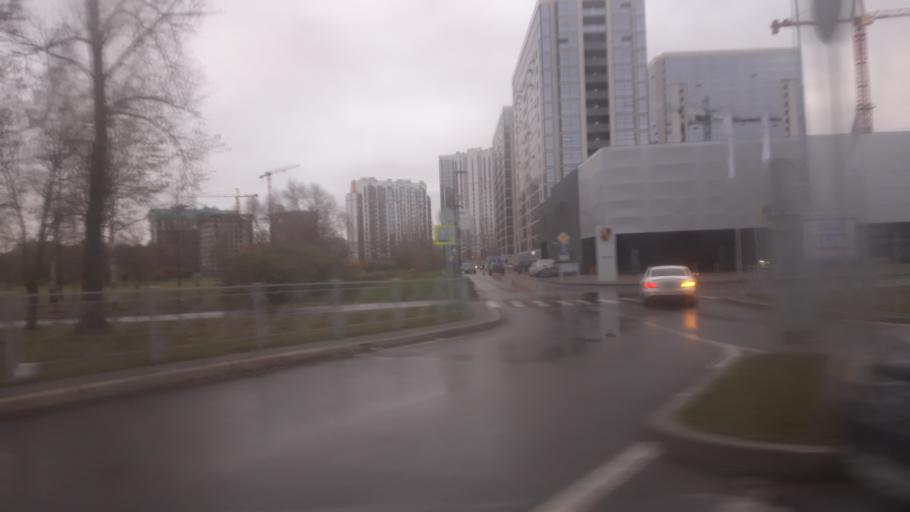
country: RU
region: St.-Petersburg
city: Kupchino
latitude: 59.8323
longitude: 30.3229
